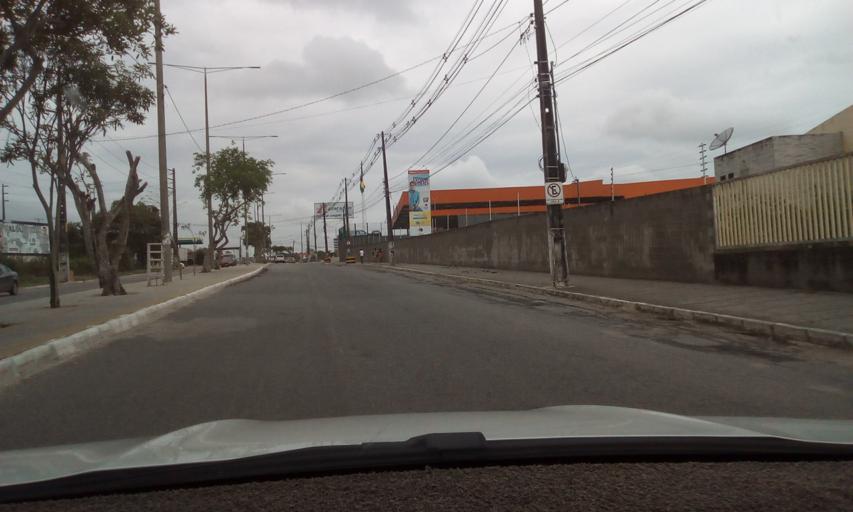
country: BR
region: Paraiba
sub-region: Campina Grande
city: Campina Grande
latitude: -7.2028
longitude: -35.8754
